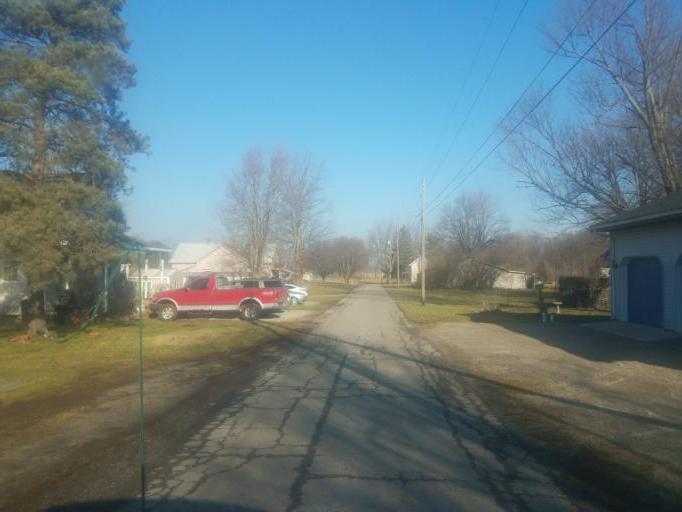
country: US
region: Ohio
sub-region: Seneca County
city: Tiffin
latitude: 41.0530
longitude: -83.0126
